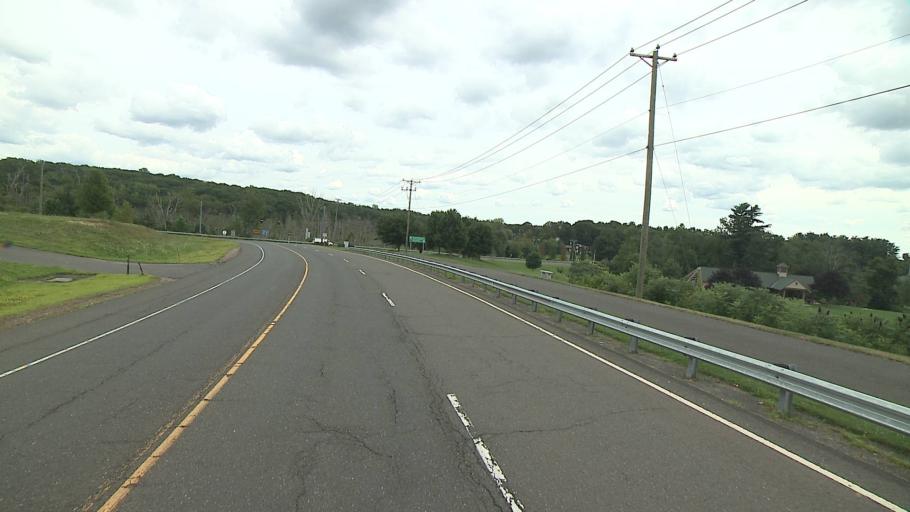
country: US
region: Connecticut
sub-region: New Haven County
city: Middlebury
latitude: 41.5220
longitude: -73.1373
